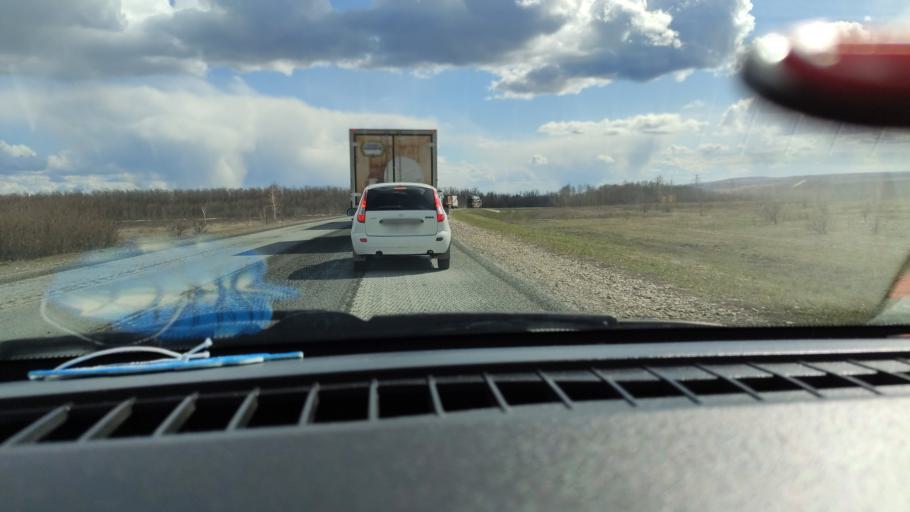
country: RU
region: Saratov
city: Dukhovnitskoye
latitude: 52.7121
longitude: 48.2663
